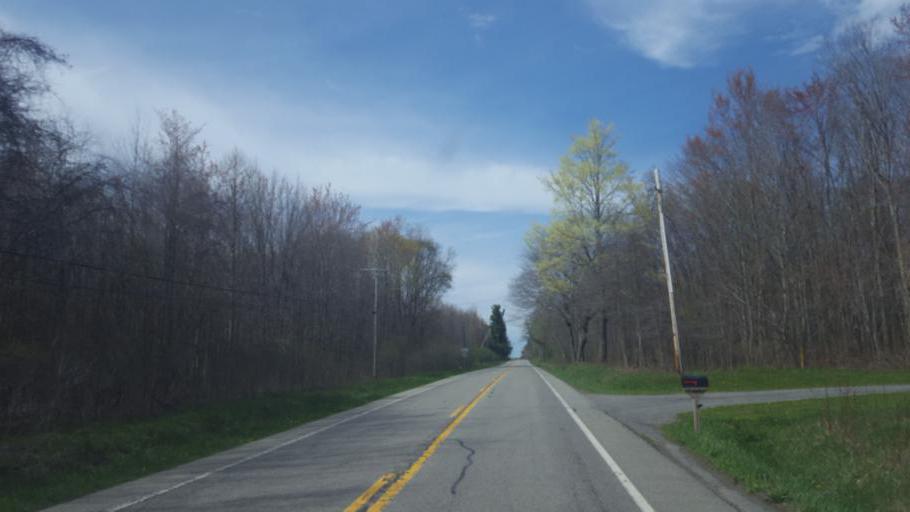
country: US
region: Pennsylvania
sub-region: Crawford County
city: Cochranton
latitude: 41.4293
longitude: -80.0747
